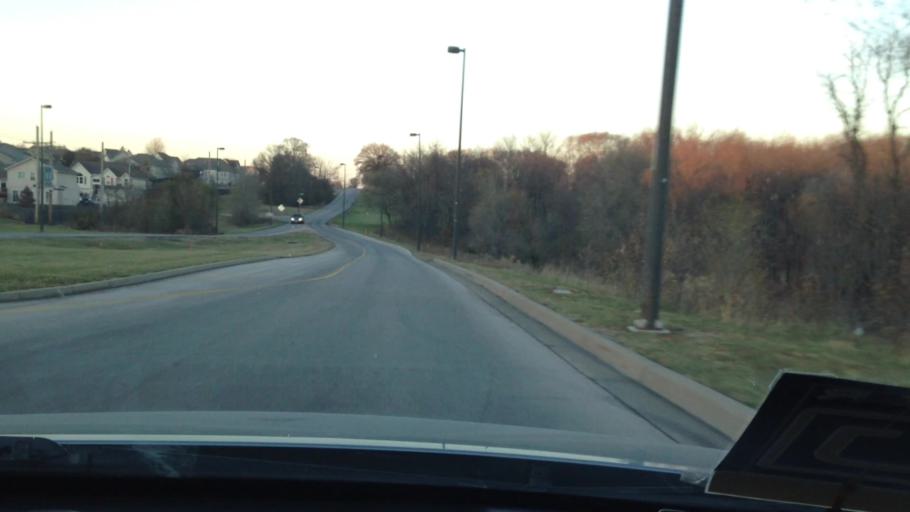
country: US
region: Missouri
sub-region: Clay County
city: Gladstone
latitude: 39.2676
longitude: -94.5570
